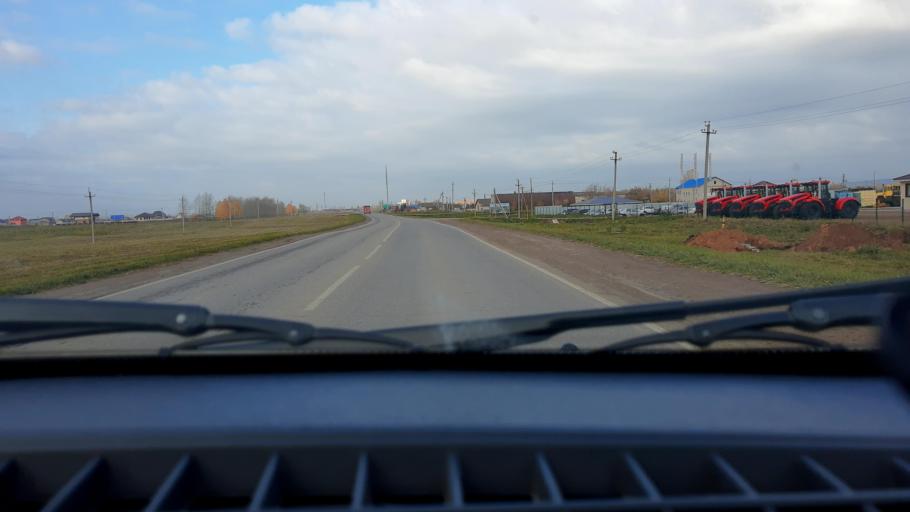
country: RU
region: Bashkortostan
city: Kabakovo
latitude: 54.5402
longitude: 56.1368
